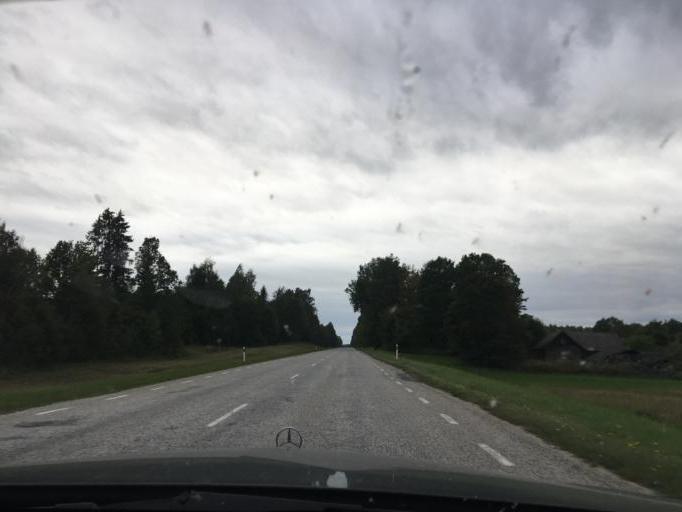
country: LV
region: Aluksnes Rajons
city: Aluksne
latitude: 57.5987
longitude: 27.1810
